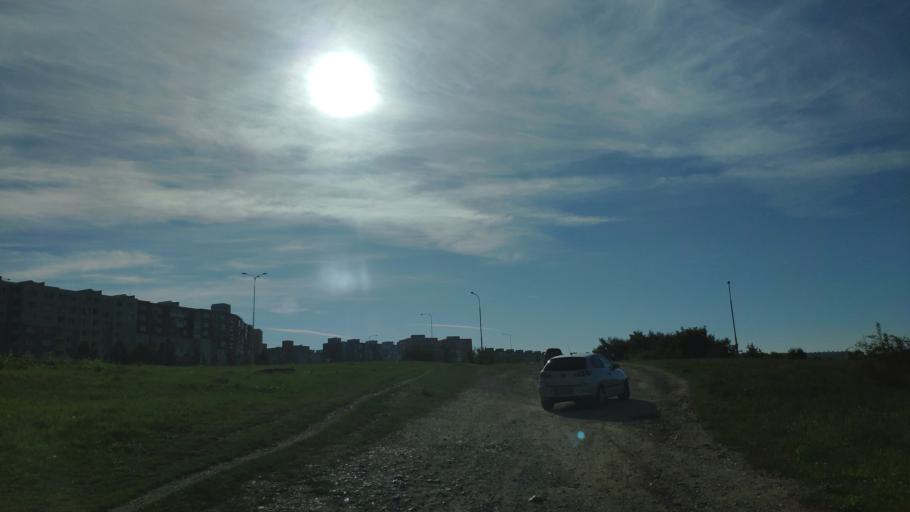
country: SK
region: Kosicky
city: Kosice
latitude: 48.7572
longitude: 21.2618
